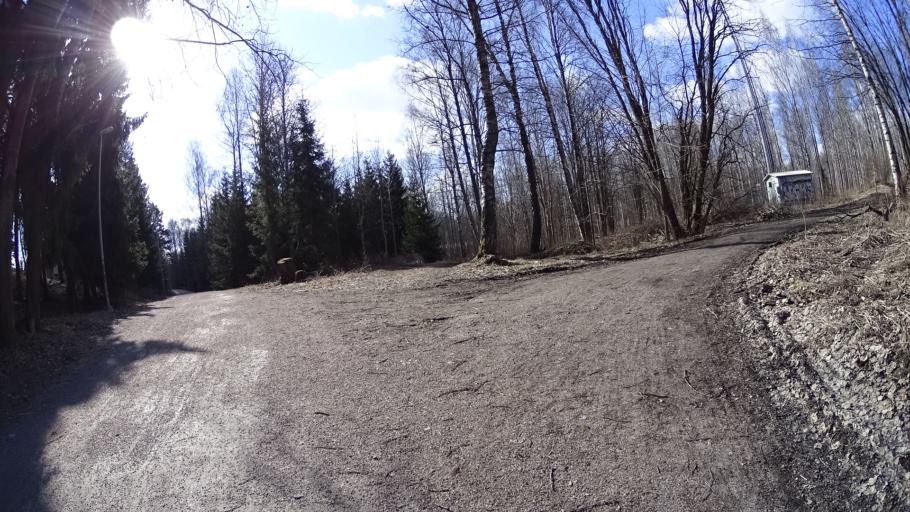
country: FI
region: Uusimaa
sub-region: Helsinki
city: Teekkarikylae
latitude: 60.2043
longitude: 24.8625
